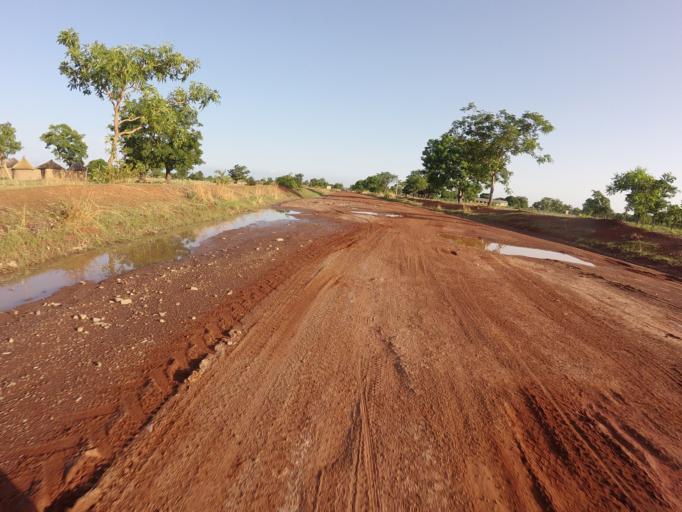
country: TG
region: Savanes
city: Sansanne-Mango
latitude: 10.3599
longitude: -0.0934
